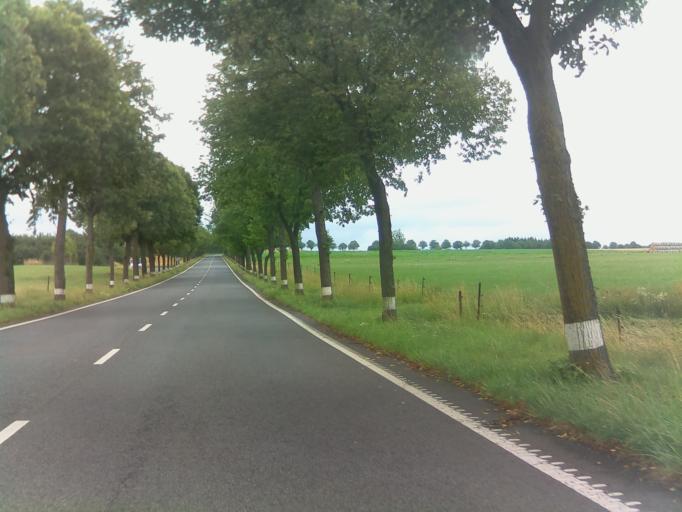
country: LU
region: Grevenmacher
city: Schengen
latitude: 49.4816
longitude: 6.3289
